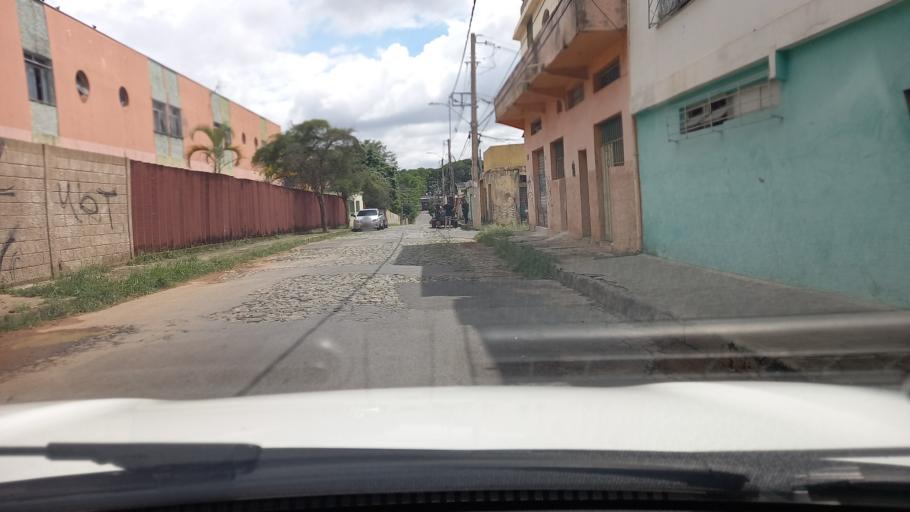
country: BR
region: Minas Gerais
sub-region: Contagem
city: Contagem
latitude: -19.9005
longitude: -44.0245
